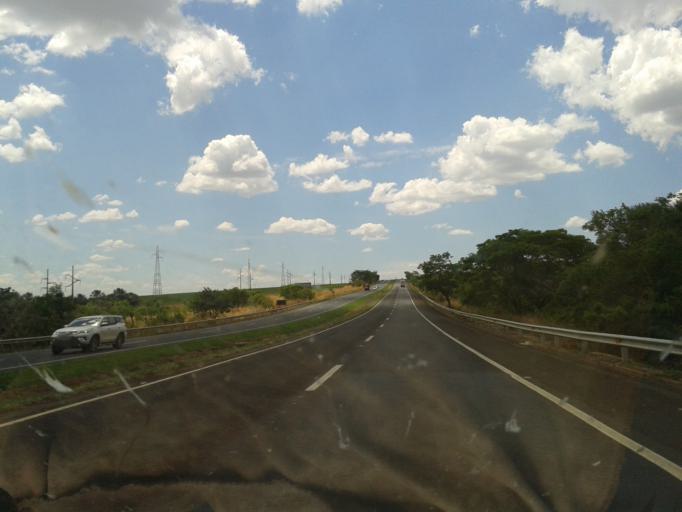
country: BR
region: Minas Gerais
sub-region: Uberlandia
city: Uberlandia
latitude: -19.0890
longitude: -48.1847
